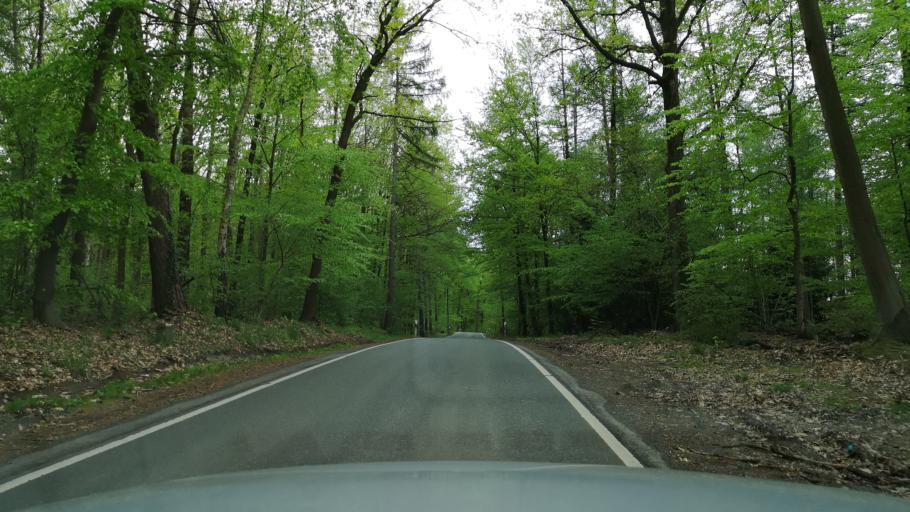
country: DE
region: North Rhine-Westphalia
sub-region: Regierungsbezirk Arnsberg
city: Frondenberg
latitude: 51.4523
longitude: 7.7095
